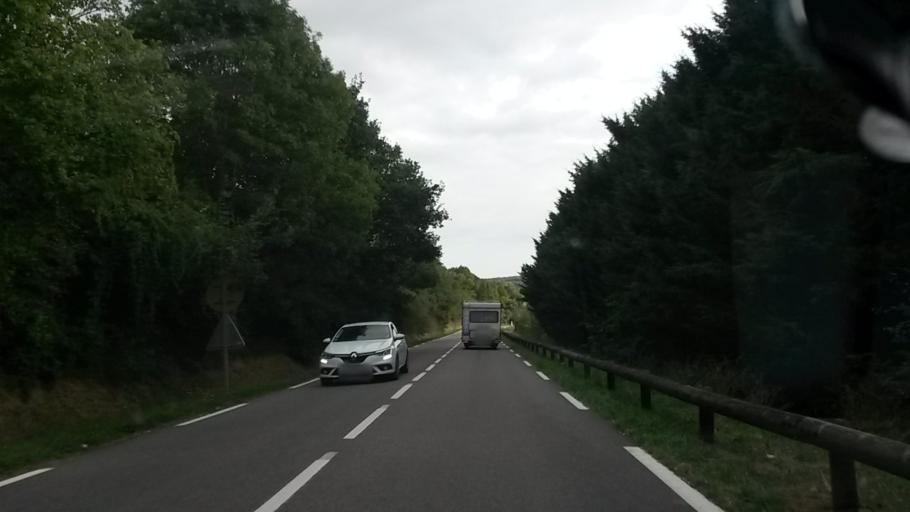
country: FR
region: Haute-Normandie
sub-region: Departement de l'Eure
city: Gravigny
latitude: 49.0645
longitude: 1.1743
